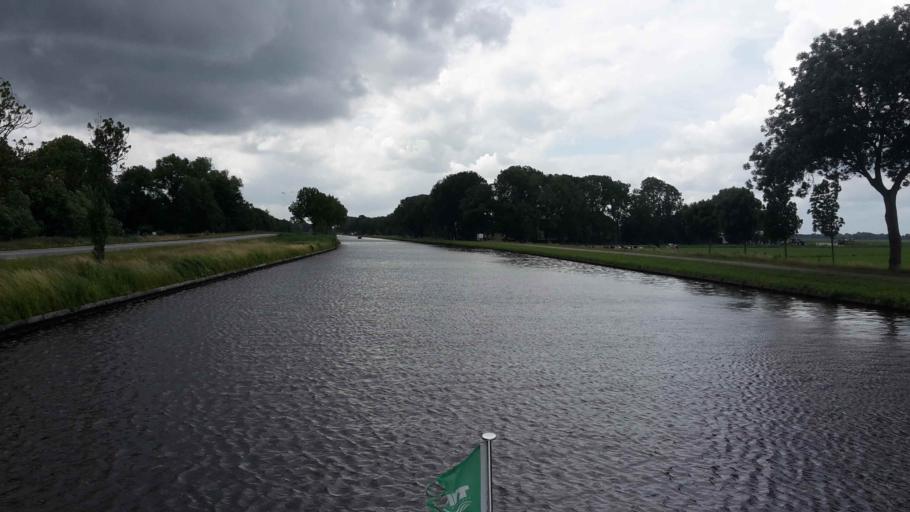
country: NL
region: Overijssel
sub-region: Gemeente Steenwijkerland
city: Giethoorn
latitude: 52.7576
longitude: 6.0802
